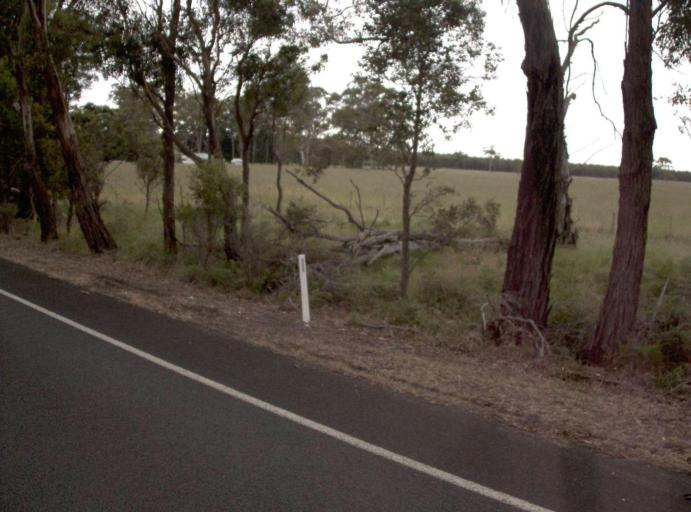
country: AU
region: Victoria
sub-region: Wellington
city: Sale
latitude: -38.4708
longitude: 146.9290
